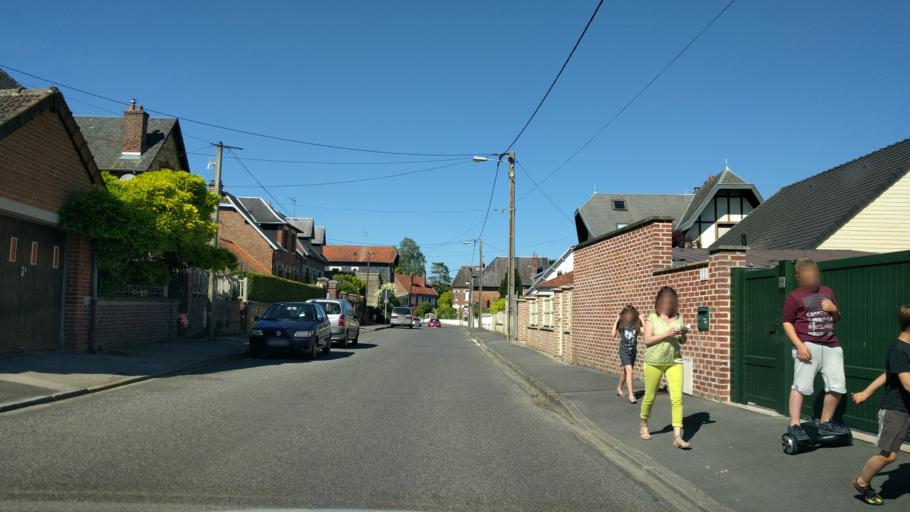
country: FR
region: Picardie
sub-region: Departement de la Somme
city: Peronne
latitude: 49.9319
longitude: 2.9295
